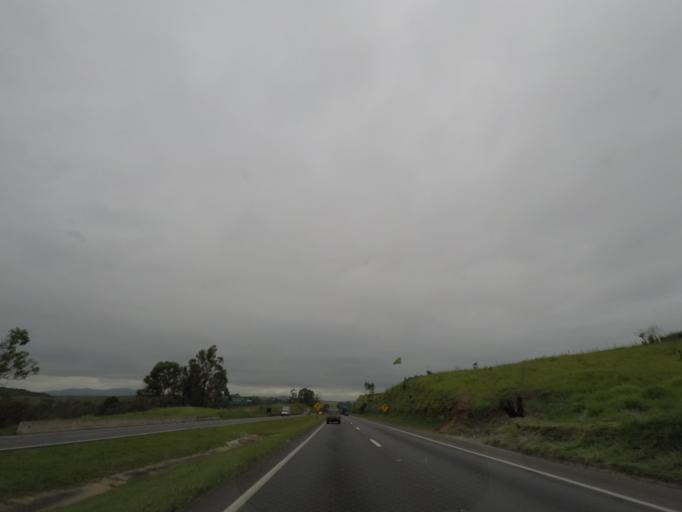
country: BR
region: Sao Paulo
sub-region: Jarinu
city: Jarinu
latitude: -23.0359
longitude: -46.7164
